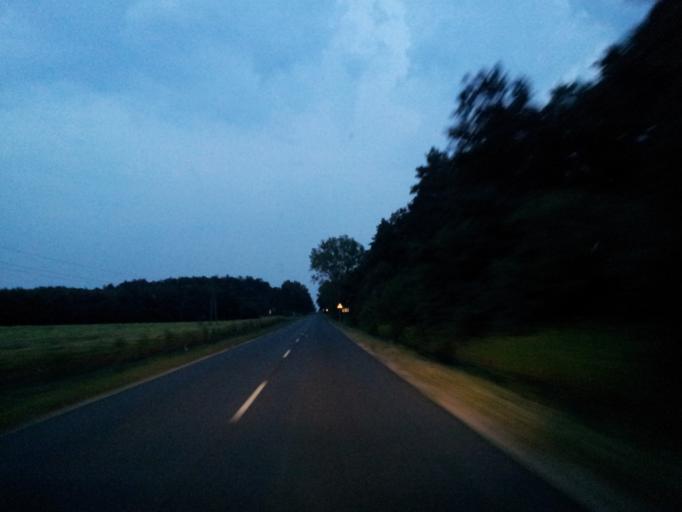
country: HU
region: Veszprem
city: Sumeg
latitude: 46.9648
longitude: 17.3259
